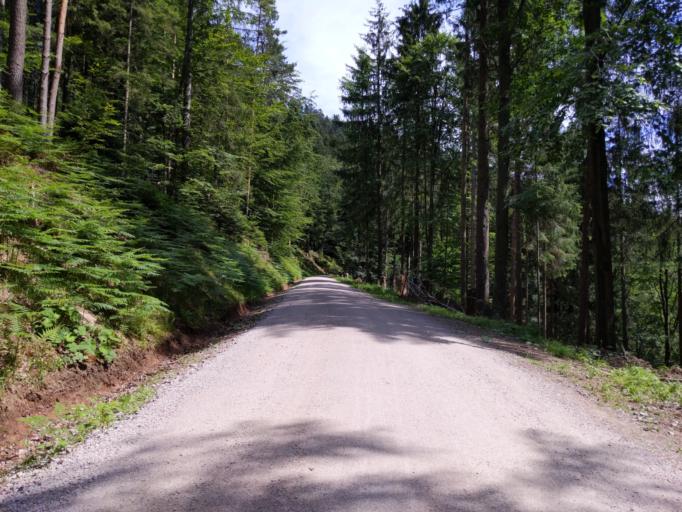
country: DE
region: Baden-Wuerttemberg
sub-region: Karlsruhe Region
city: Bad Rippoldsau-Schapbach
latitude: 48.4134
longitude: 8.3637
